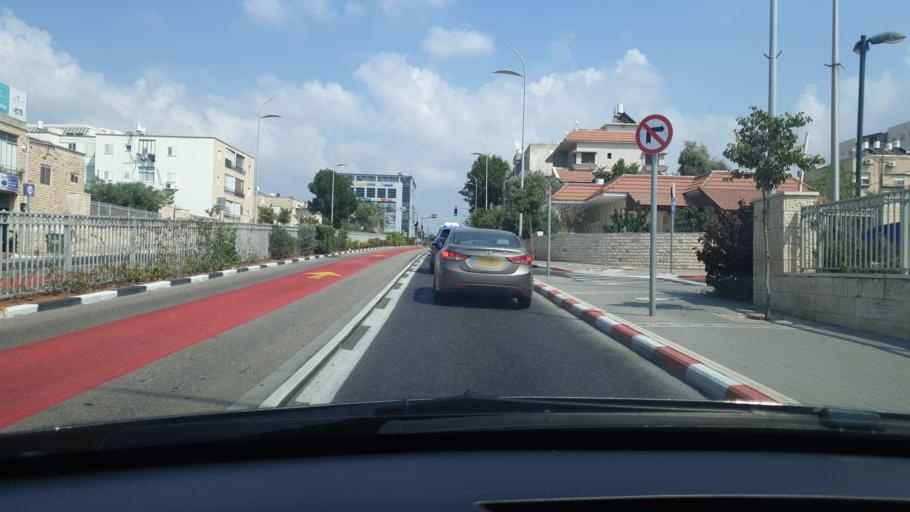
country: IL
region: Haifa
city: Qiryat Ata
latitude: 32.8126
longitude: 35.1022
